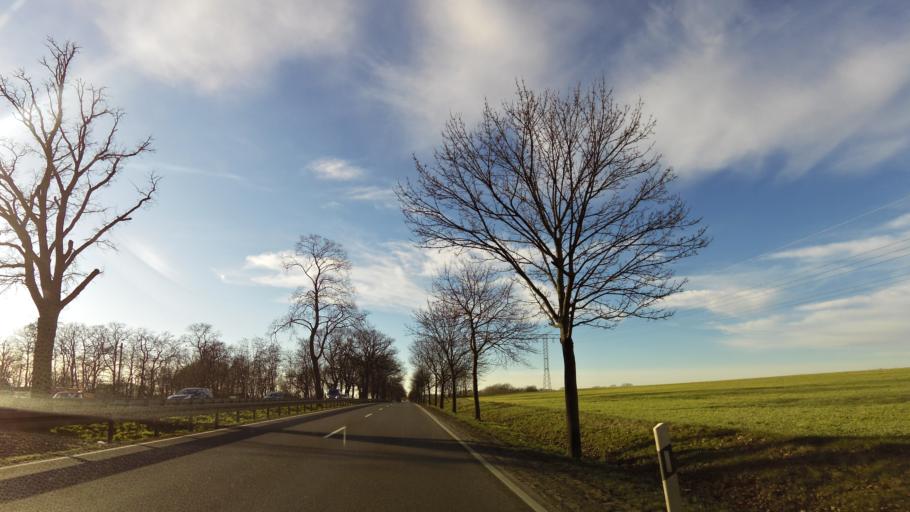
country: DE
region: Brandenburg
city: Schoneiche
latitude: 52.5008
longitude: 13.7149
